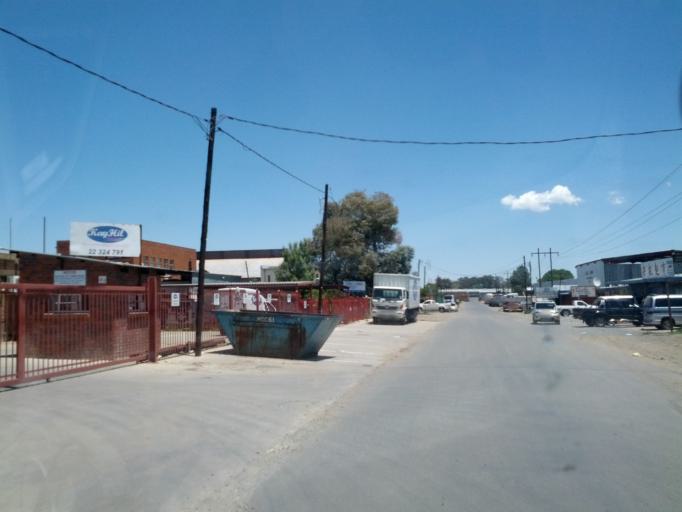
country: LS
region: Maseru
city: Maseru
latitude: -29.2957
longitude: 27.4765
